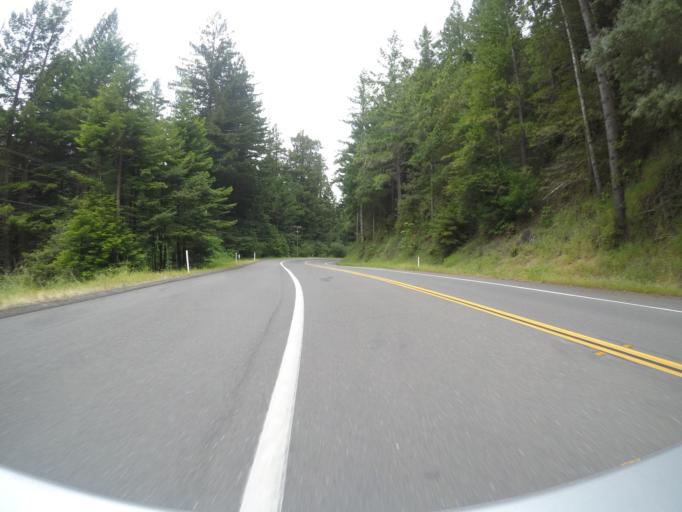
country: US
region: California
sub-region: Humboldt County
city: Rio Dell
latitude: 40.4037
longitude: -123.9510
